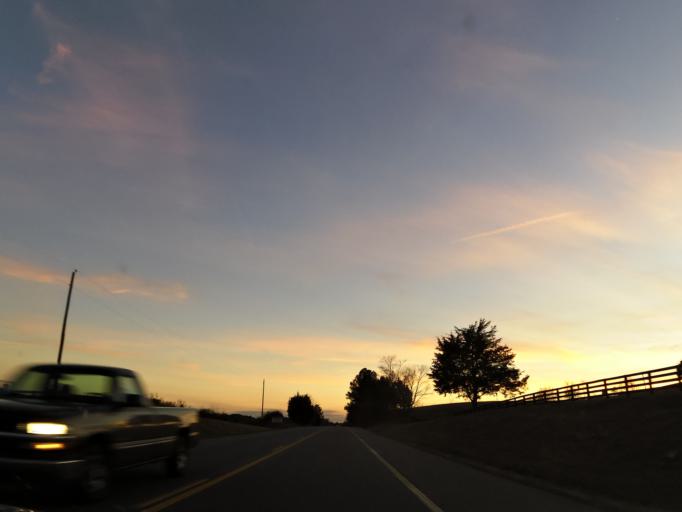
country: US
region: Tennessee
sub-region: Bradley County
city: Wildwood Lake
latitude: 35.0548
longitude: -84.8992
